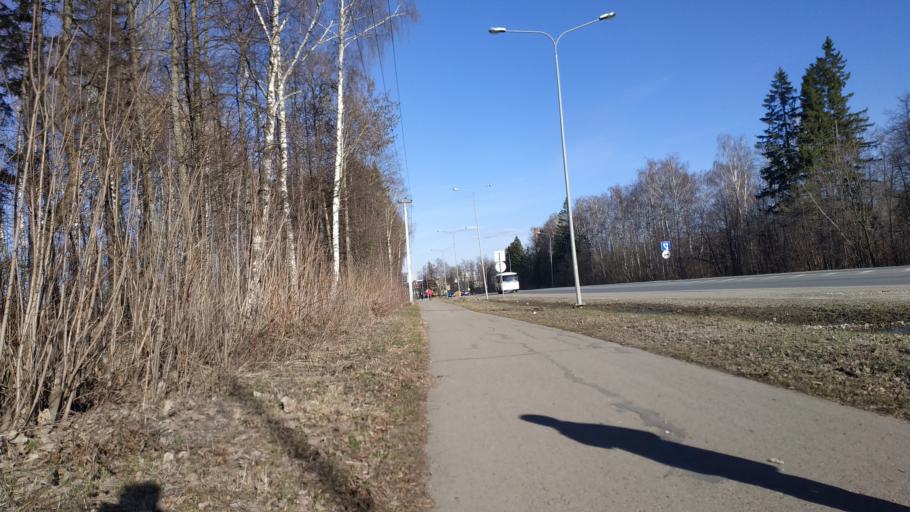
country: RU
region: Chuvashia
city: Novyye Lapsary
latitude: 56.1302
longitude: 47.1550
